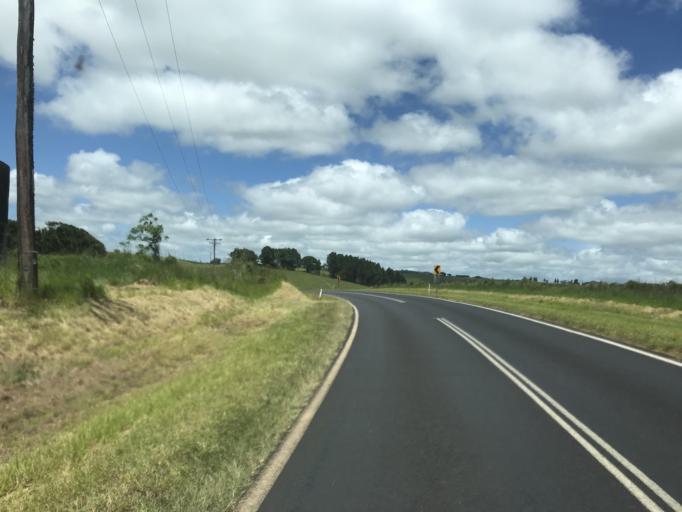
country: AU
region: Queensland
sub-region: Tablelands
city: Ravenshoe
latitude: -17.5089
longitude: 145.4741
